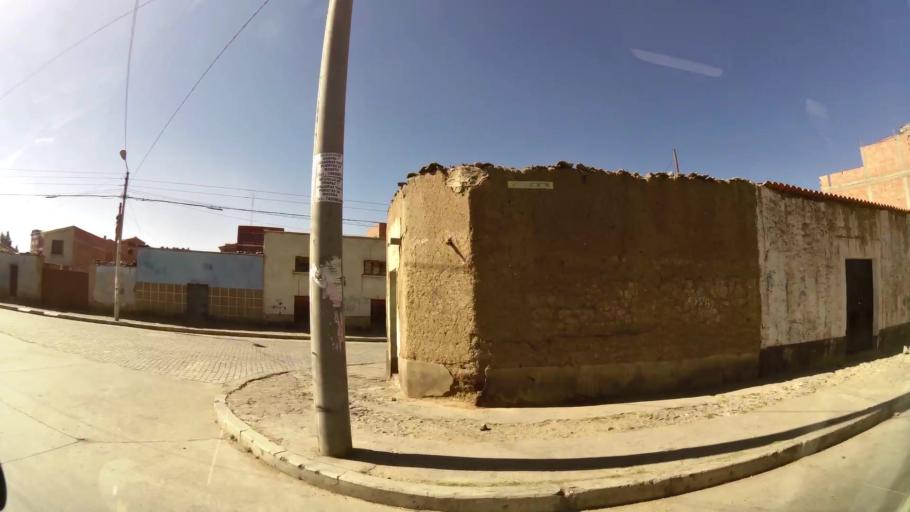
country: BO
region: La Paz
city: La Paz
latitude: -16.5162
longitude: -68.1626
